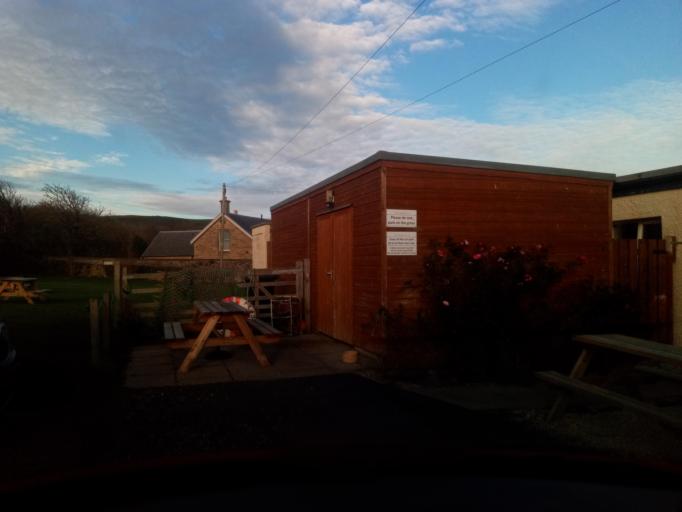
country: GB
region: Scotland
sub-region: The Scottish Borders
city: Eyemouth
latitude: 55.8993
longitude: -2.1327
